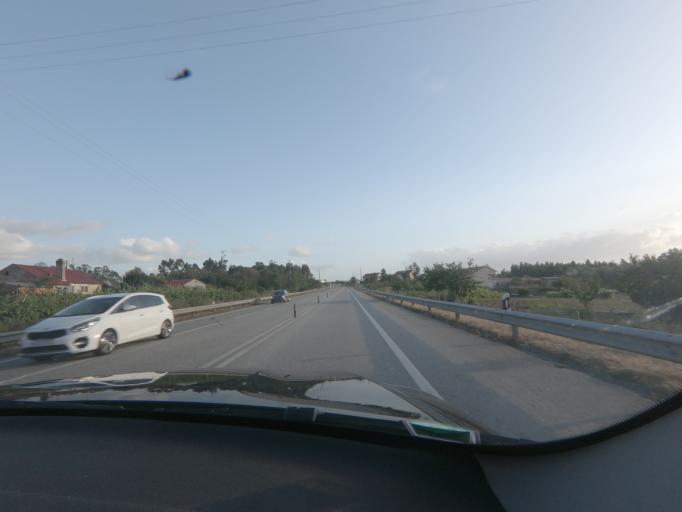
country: PT
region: Viseu
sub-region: Santa Comba Dao
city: Santa Comba Dao
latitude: 40.3658
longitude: -8.1320
